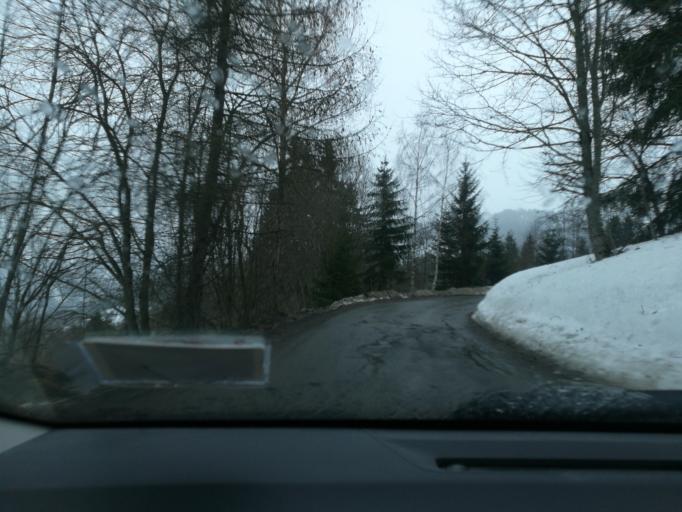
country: FR
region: Rhone-Alpes
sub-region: Departement de la Haute-Savoie
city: Saint-Gervais-les-Bains
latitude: 45.8676
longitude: 6.6919
